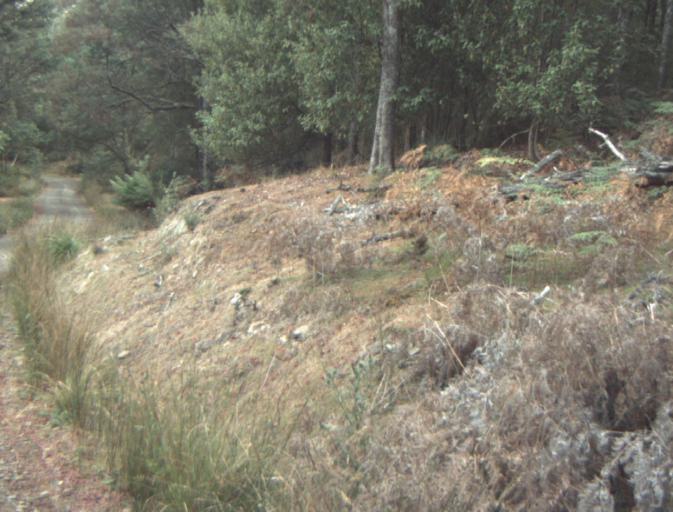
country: AU
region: Tasmania
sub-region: Launceston
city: Mayfield
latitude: -41.2801
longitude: 147.2330
